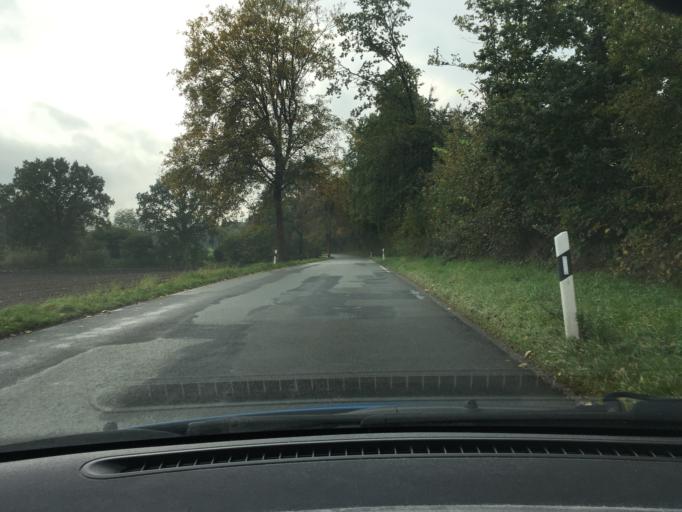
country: DE
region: Schleswig-Holstein
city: Tensfeld
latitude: 54.0363
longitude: 10.3120
